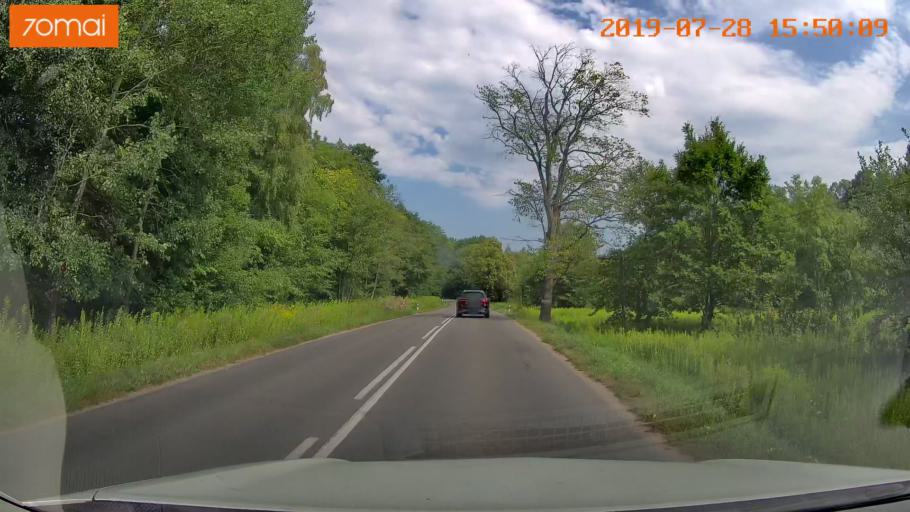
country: RU
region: Kaliningrad
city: Otradnoye
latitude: 54.9397
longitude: 20.0877
